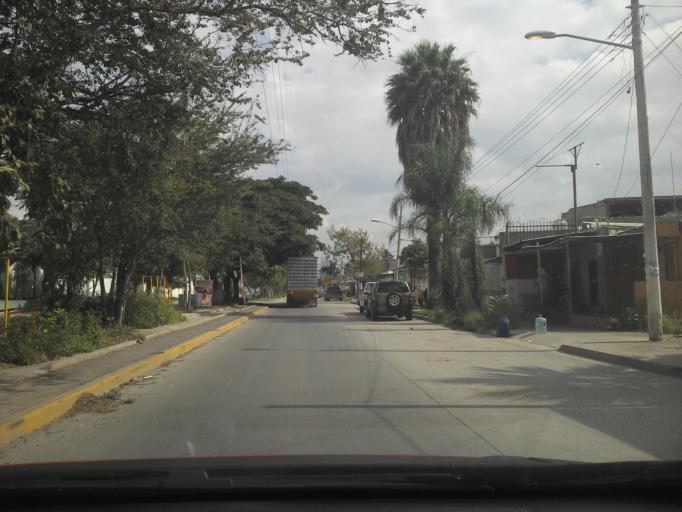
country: MX
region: Jalisco
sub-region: Tlajomulco de Zuniga
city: Altus Bosques
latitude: 20.5823
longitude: -103.3527
